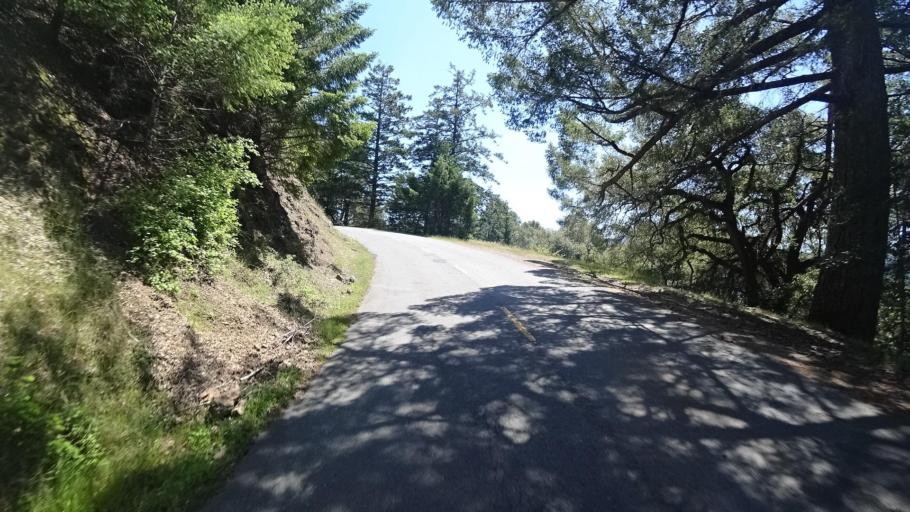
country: US
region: California
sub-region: Humboldt County
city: Rio Dell
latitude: 40.2538
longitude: -124.1193
